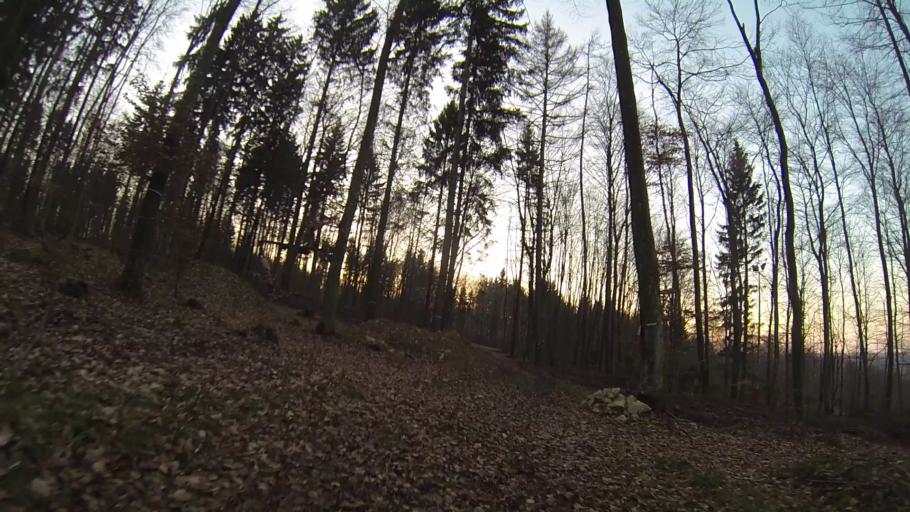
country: DE
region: Baden-Wuerttemberg
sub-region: Regierungsbezirk Stuttgart
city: Heidenheim an der Brenz
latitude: 48.6730
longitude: 10.1160
